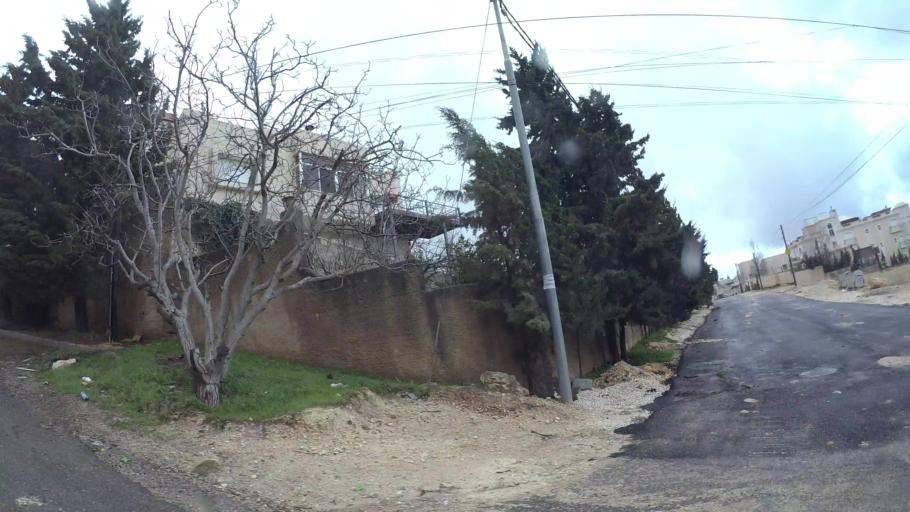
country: JO
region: Amman
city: Al Jubayhah
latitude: 32.0347
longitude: 35.8564
